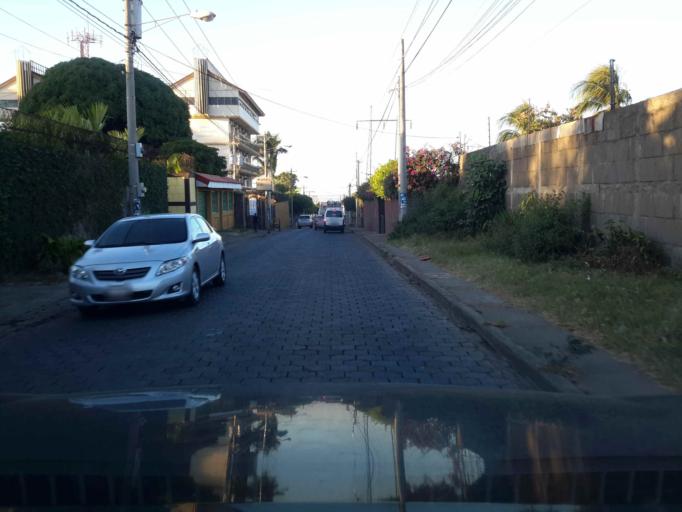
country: NI
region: Managua
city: Managua
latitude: 12.1004
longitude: -86.2327
